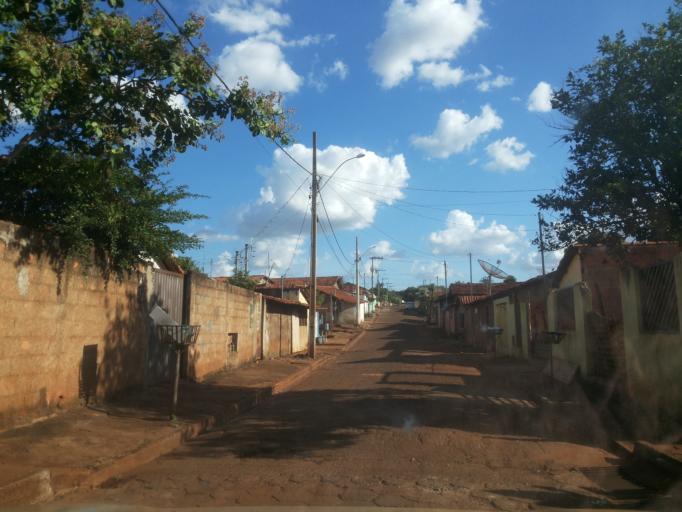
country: BR
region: Minas Gerais
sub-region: Capinopolis
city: Capinopolis
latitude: -18.6833
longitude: -49.5753
